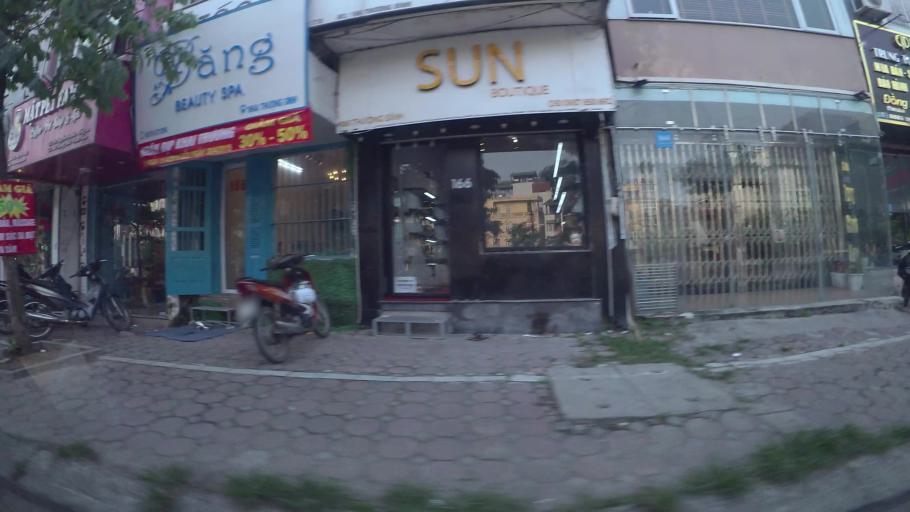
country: VN
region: Ha Noi
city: Thanh Xuan
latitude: 20.9979
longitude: 105.8163
